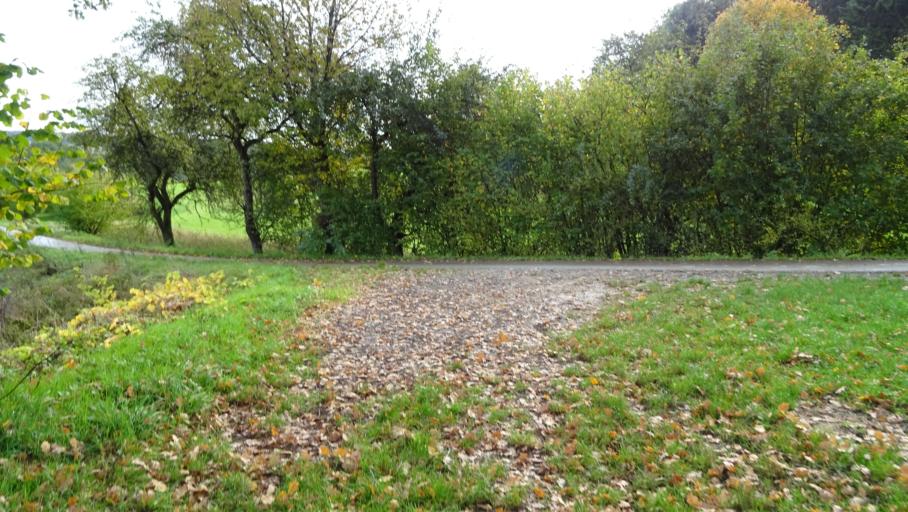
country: DE
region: Baden-Wuerttemberg
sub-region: Karlsruhe Region
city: Billigheim
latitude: 49.3329
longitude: 9.2280
